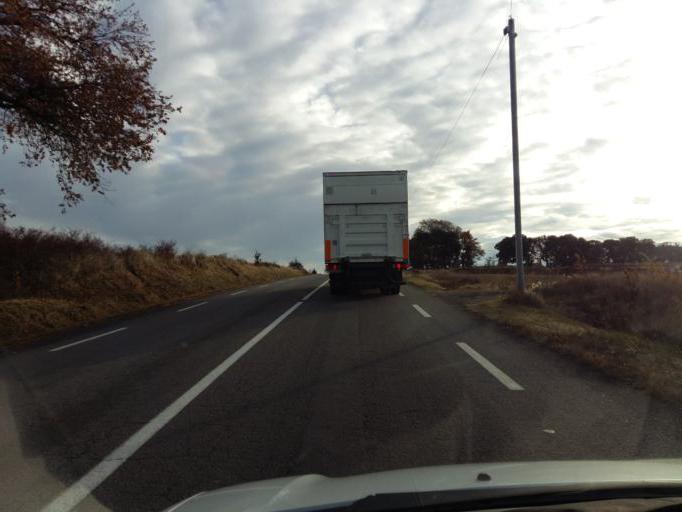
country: FR
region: Rhone-Alpes
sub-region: Departement de la Drome
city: Tulette
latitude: 44.2936
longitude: 4.9429
